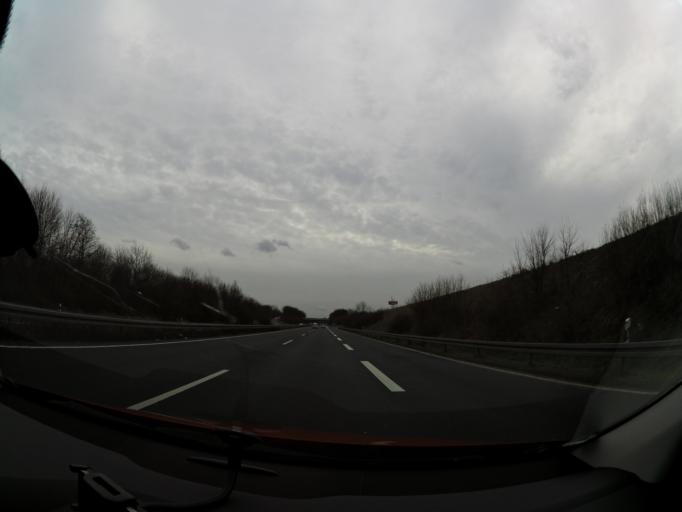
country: DE
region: Lower Saxony
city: Leiferde
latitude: 52.2198
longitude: 10.5333
